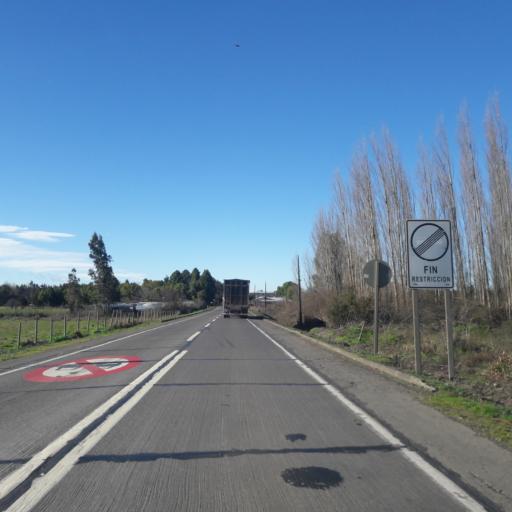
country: CL
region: Araucania
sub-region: Provincia de Malleco
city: Angol
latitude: -37.7752
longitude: -72.5439
